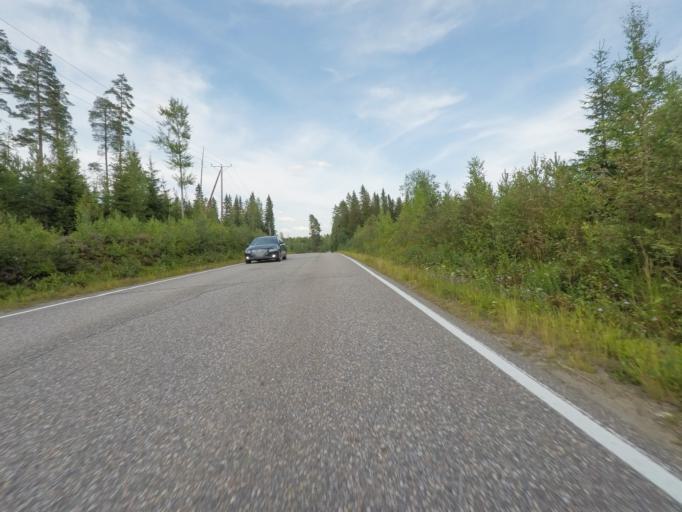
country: FI
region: Southern Savonia
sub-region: Savonlinna
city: Sulkava
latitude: 61.7497
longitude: 28.2068
